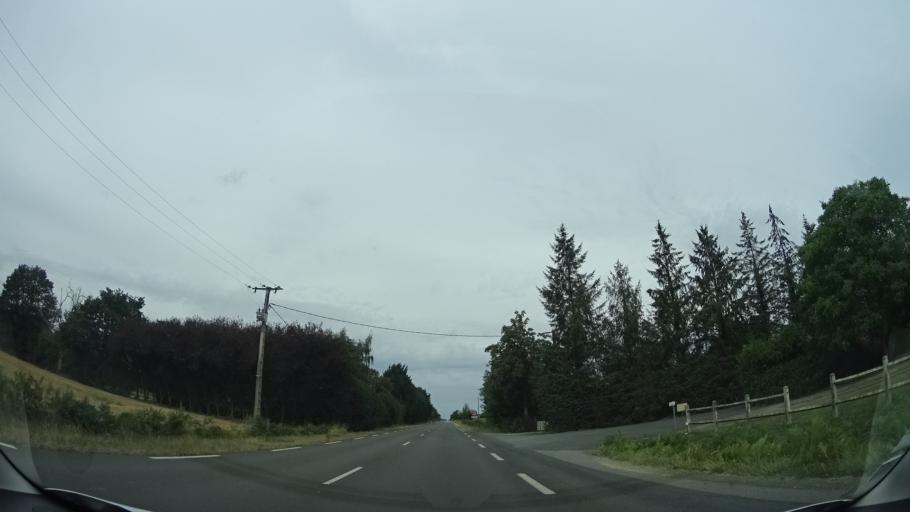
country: FR
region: Pays de la Loire
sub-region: Departement de la Mayenne
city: Meslay-du-Maine
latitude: 47.9631
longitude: -0.5772
